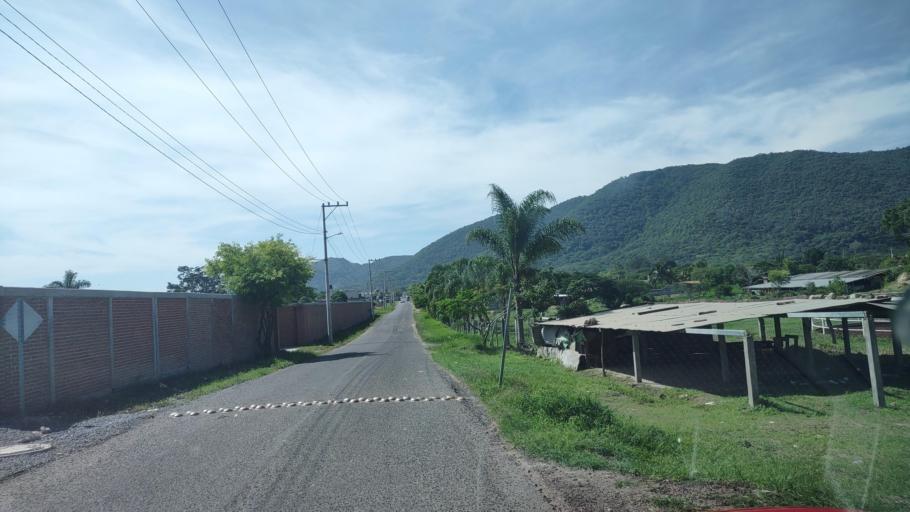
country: MX
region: Veracruz
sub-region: Emiliano Zapata
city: Dos Rios
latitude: 19.4317
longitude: -96.8023
